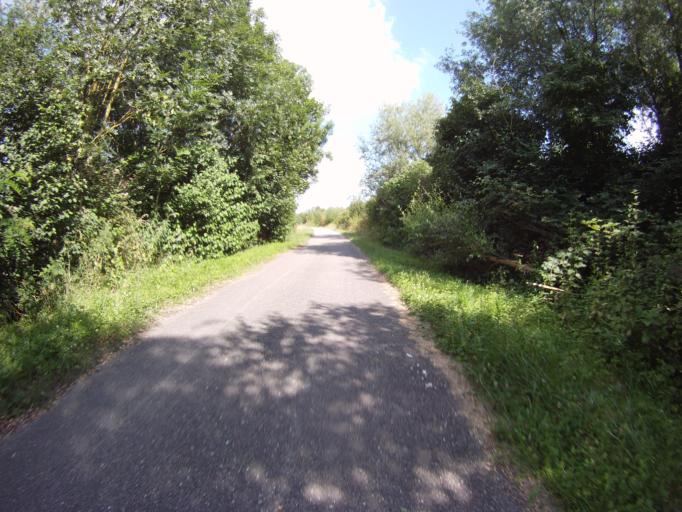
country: FR
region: Lorraine
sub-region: Departement de Meurthe-et-Moselle
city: Bouxieres-aux-Dames
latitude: 48.7461
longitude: 6.1617
